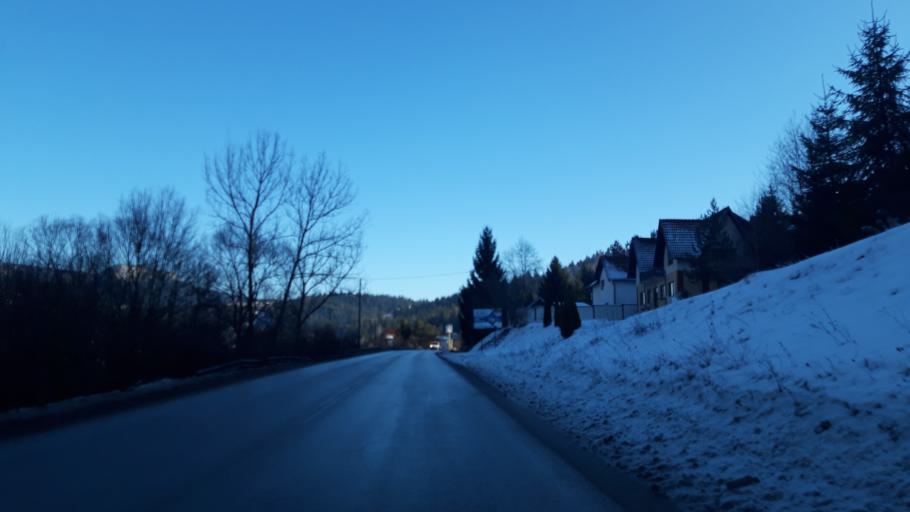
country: BA
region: Republika Srpska
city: Pale
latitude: 43.8480
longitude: 18.5477
